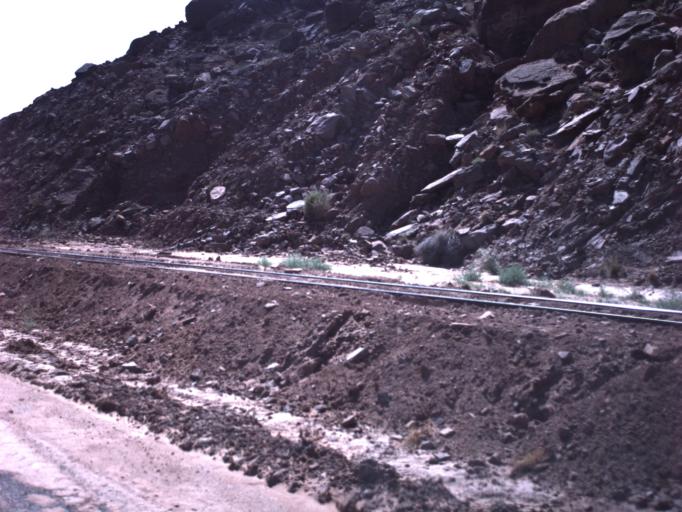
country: US
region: Utah
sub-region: Grand County
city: Moab
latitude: 38.5380
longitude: -109.6552
